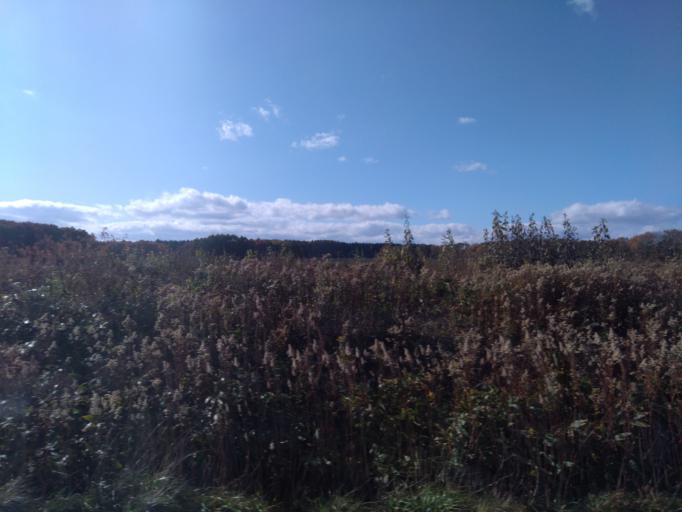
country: JP
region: Hokkaido
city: Kitahiroshima
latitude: 42.9517
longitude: 141.5707
